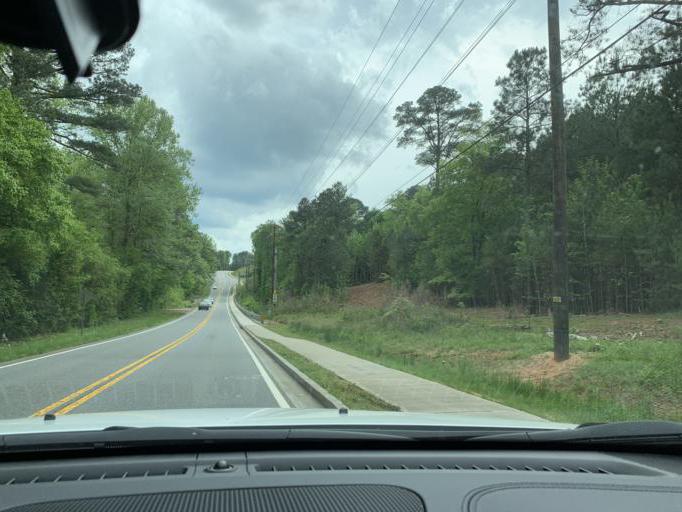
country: US
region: Georgia
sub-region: Gwinnett County
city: Sugar Hill
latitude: 34.1263
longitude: -84.1021
